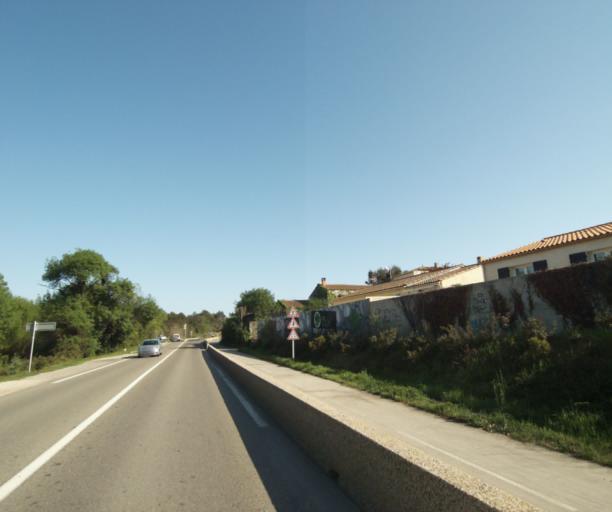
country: FR
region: Languedoc-Roussillon
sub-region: Departement de l'Herault
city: Jacou
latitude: 43.6611
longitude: 3.9275
